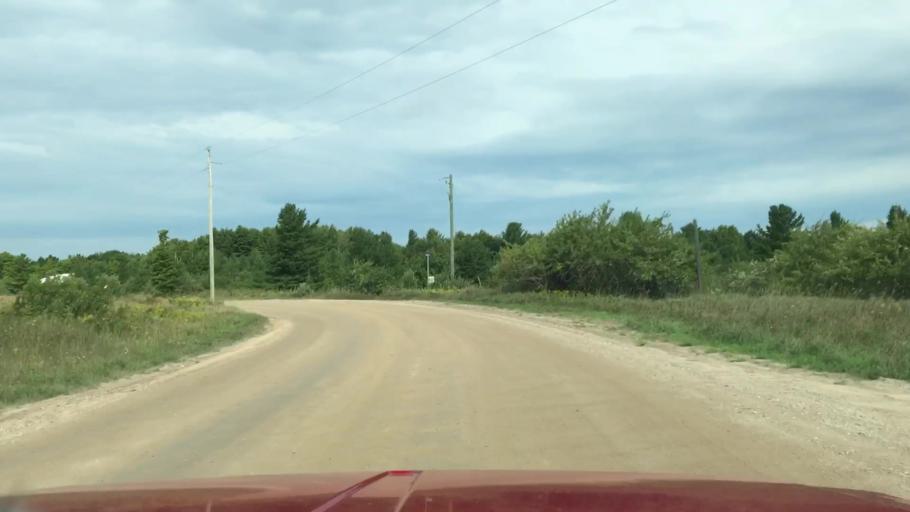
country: US
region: Michigan
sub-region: Charlevoix County
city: Charlevoix
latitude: 45.7282
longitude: -85.5164
